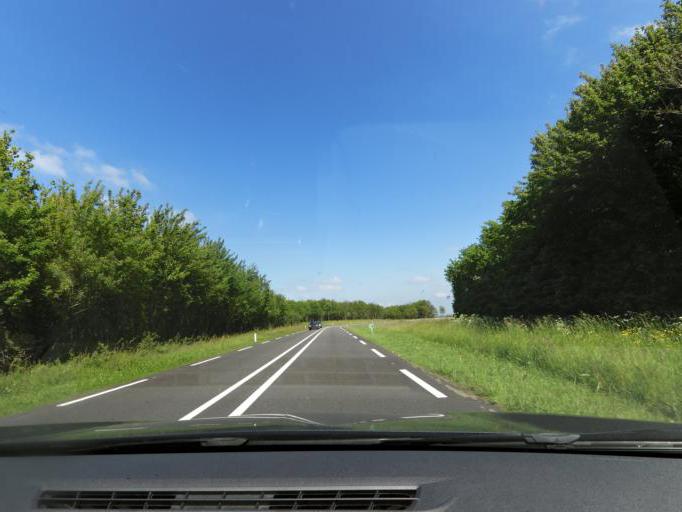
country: NL
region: South Holland
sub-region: Gemeente Hellevoetsluis
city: Nieuw-Helvoet
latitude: 51.8478
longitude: 4.0911
